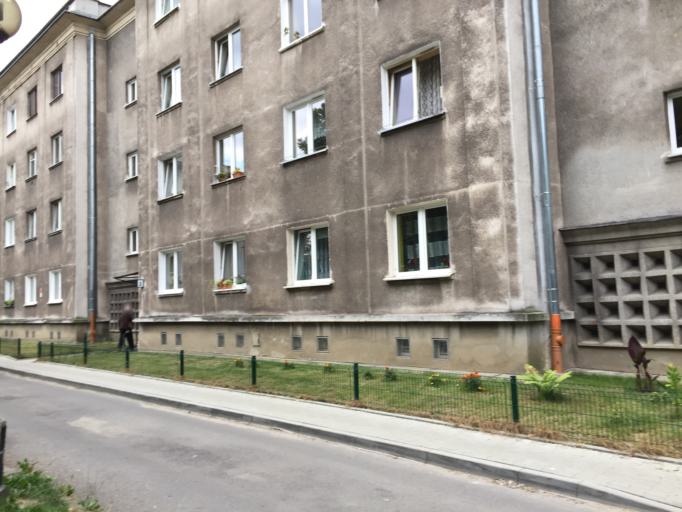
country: PL
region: Lesser Poland Voivodeship
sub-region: Powiat wielicki
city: Kokotow
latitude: 50.0804
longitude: 20.0356
